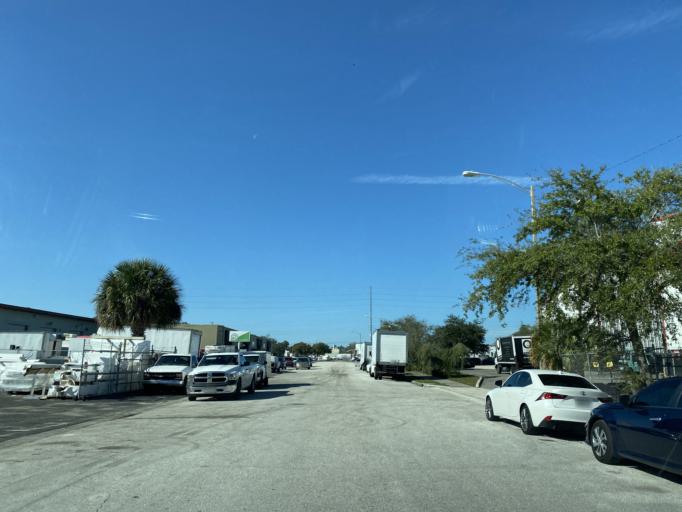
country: US
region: Florida
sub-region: Orange County
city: Holden Heights
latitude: 28.5150
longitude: -81.3824
